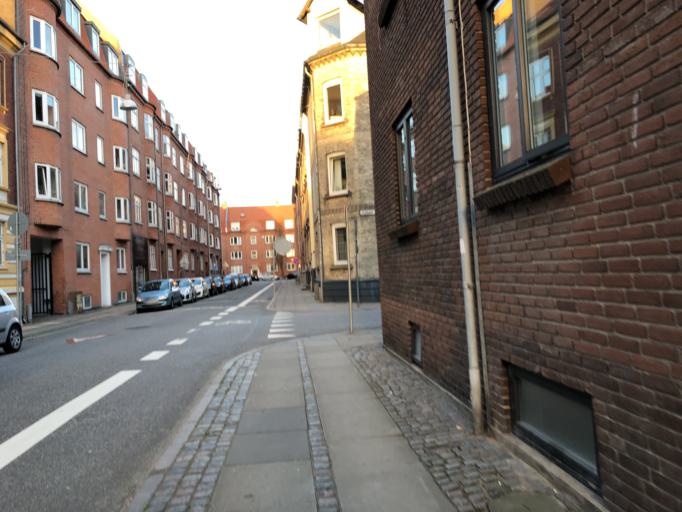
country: DK
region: North Denmark
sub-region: Alborg Kommune
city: Aalborg
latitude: 57.0506
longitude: 9.9109
